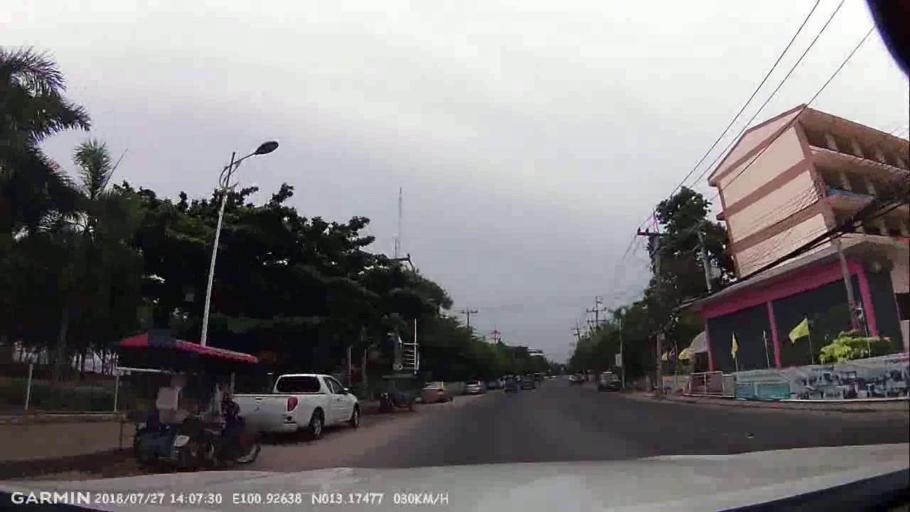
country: TH
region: Chon Buri
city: Si Racha
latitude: 13.1749
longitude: 100.9264
